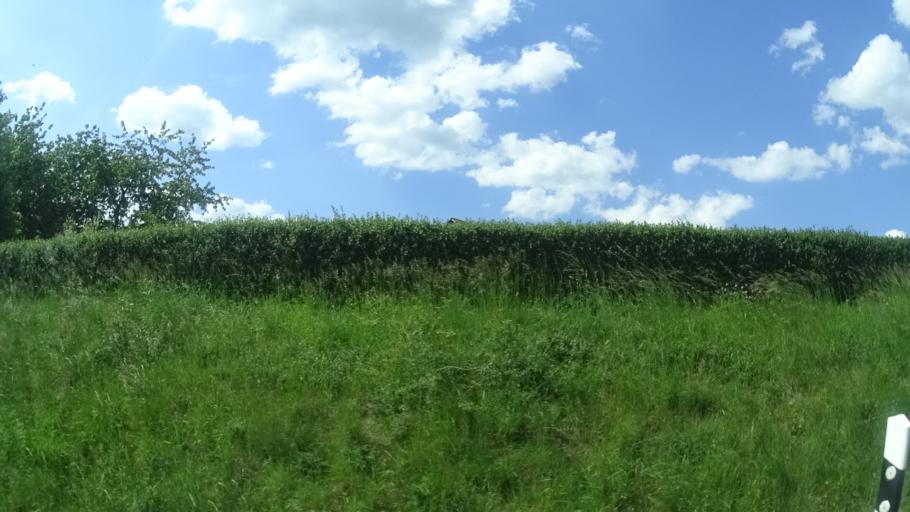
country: DE
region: Hesse
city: Tann
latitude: 50.6374
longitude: 10.0243
